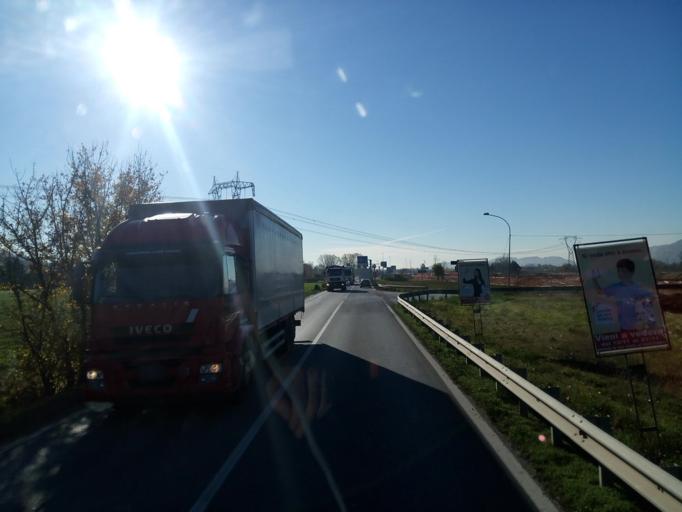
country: IT
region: Veneto
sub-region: Provincia di Vicenza
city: Tezze
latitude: 45.5222
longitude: 11.3870
